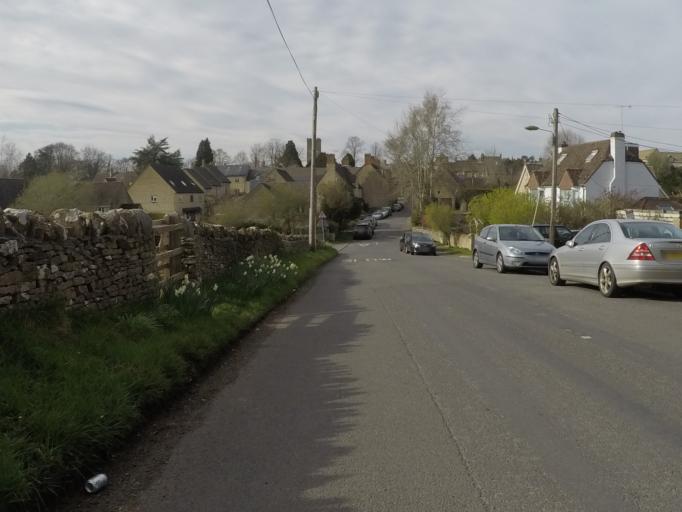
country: GB
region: England
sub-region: Oxfordshire
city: Charlbury
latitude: 51.8700
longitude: -1.4834
